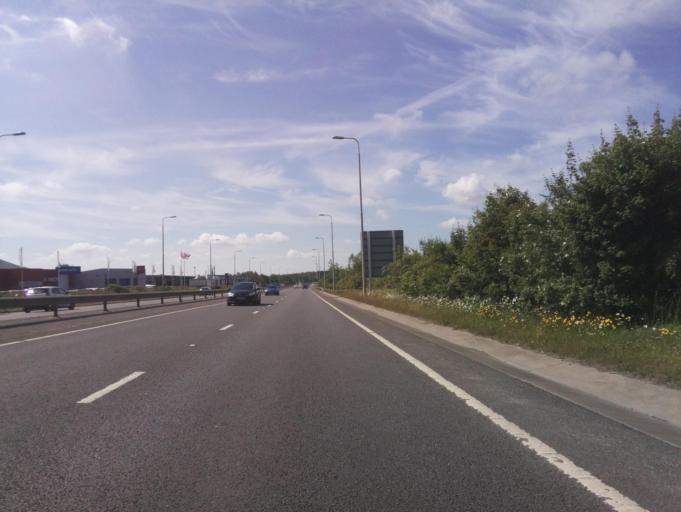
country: GB
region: England
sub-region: Lincolnshire
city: Skellingthorpe
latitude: 53.2063
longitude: -0.6178
